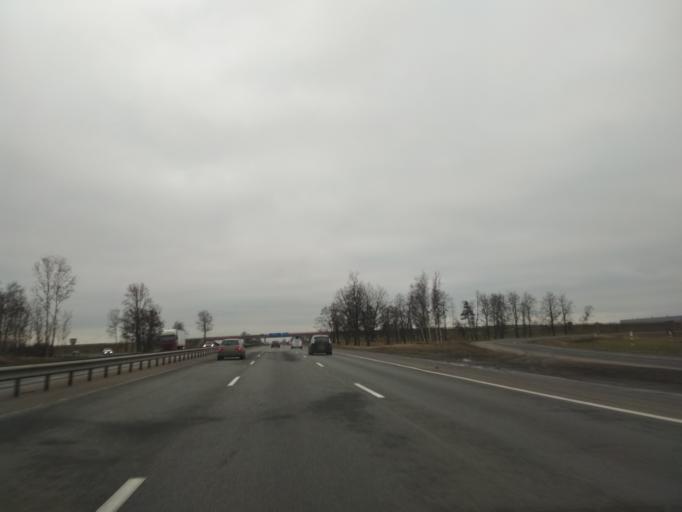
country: BY
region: Minsk
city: Pryvol'ny
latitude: 53.8071
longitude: 27.7887
